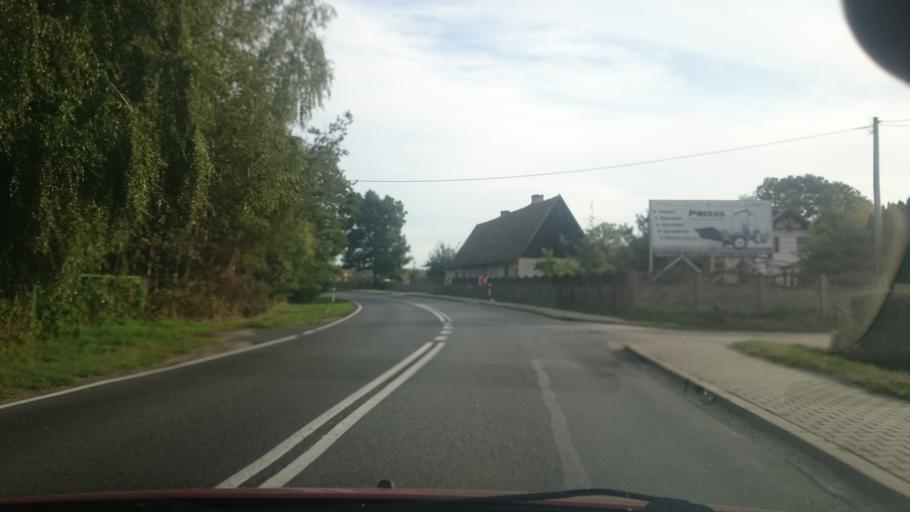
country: PL
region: Lower Silesian Voivodeship
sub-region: Powiat milicki
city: Milicz
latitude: 51.4925
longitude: 17.2850
